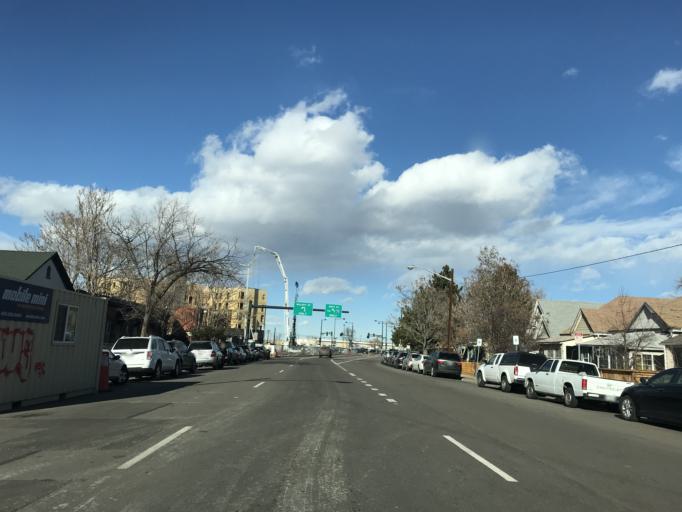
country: US
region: Colorado
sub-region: Denver County
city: Denver
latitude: 39.7685
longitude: -104.9721
